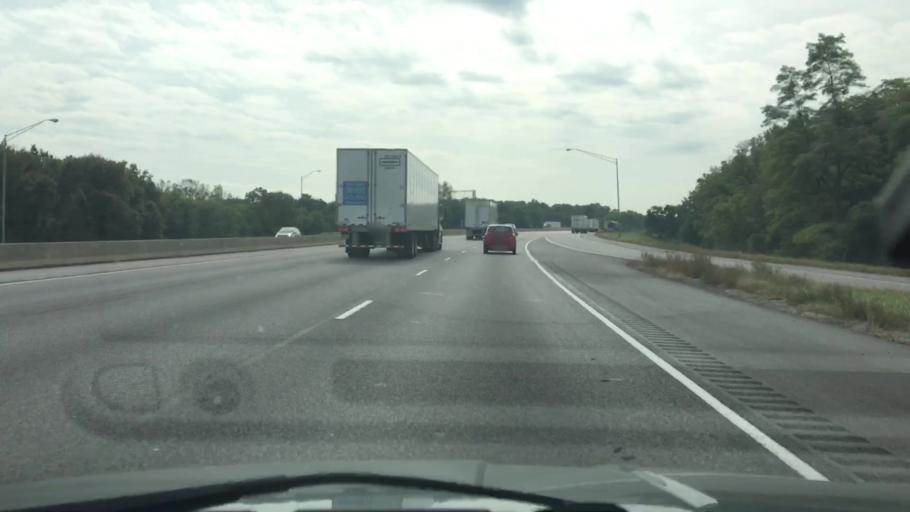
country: US
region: Indiana
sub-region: LaPorte County
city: Trail Creek
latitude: 41.6907
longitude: -86.8118
